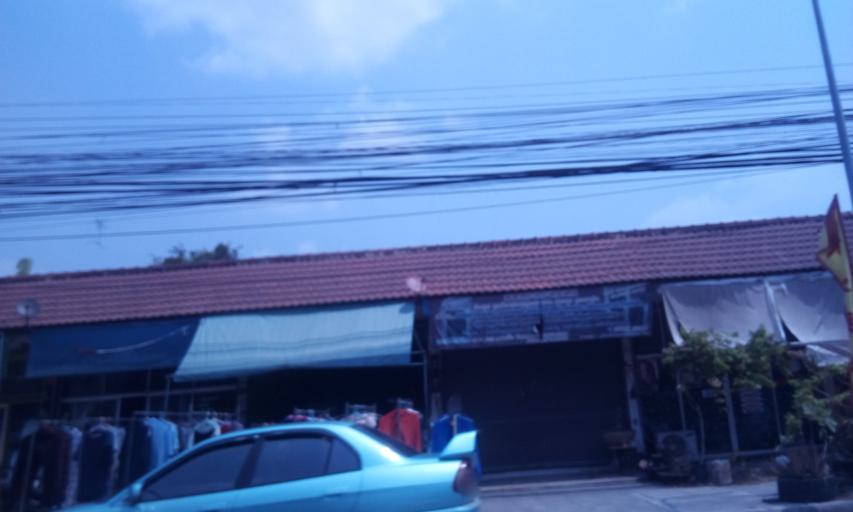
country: TH
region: Chachoengsao
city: Chachoengsao
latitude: 13.7029
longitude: 101.0916
